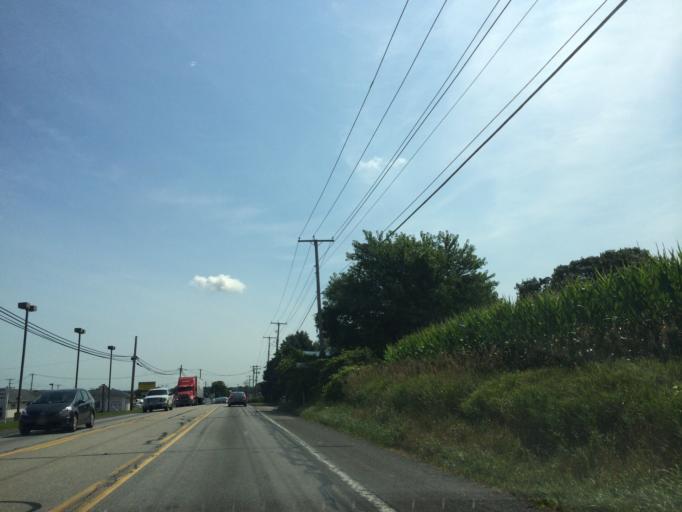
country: US
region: Pennsylvania
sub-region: Berks County
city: Fleetwood
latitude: 40.4837
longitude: -75.8436
